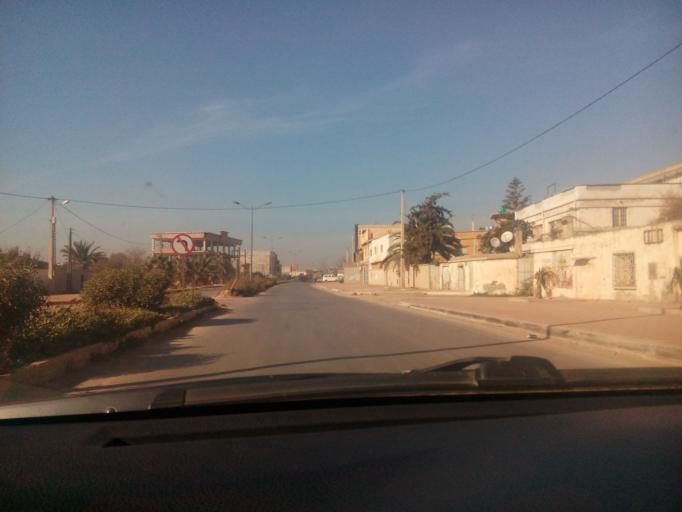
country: DZ
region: Oran
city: Es Senia
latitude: 35.6461
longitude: -0.6101
